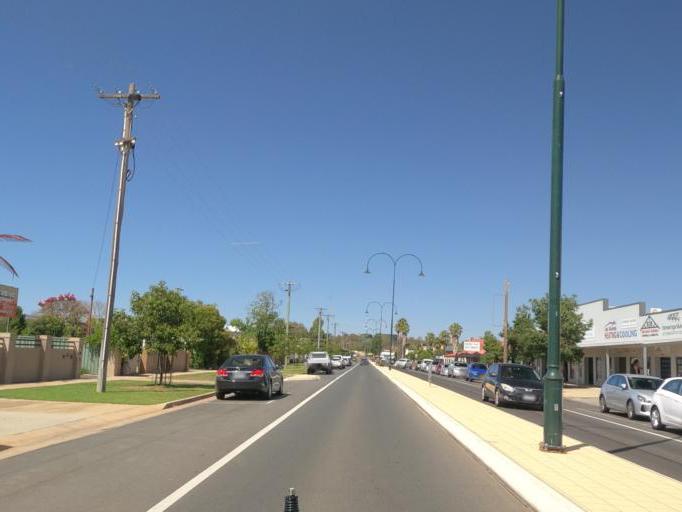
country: AU
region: New South Wales
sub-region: Corowa Shire
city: Mulwala
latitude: -35.9902
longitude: 146.0045
